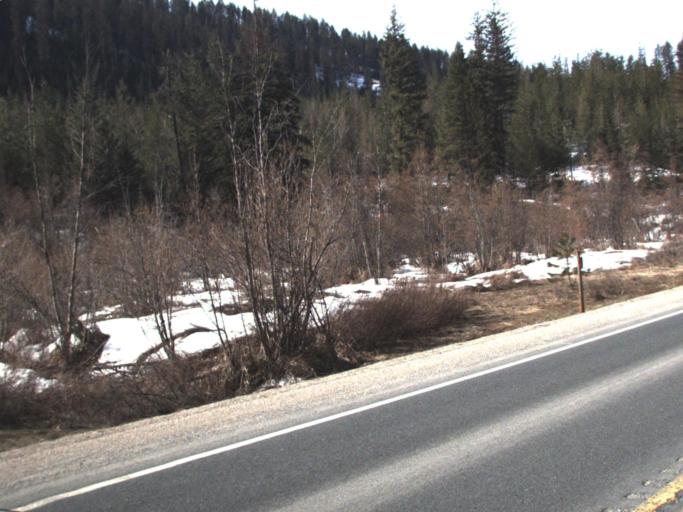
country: US
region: Washington
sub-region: Stevens County
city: Chewelah
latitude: 48.5318
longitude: -117.6184
